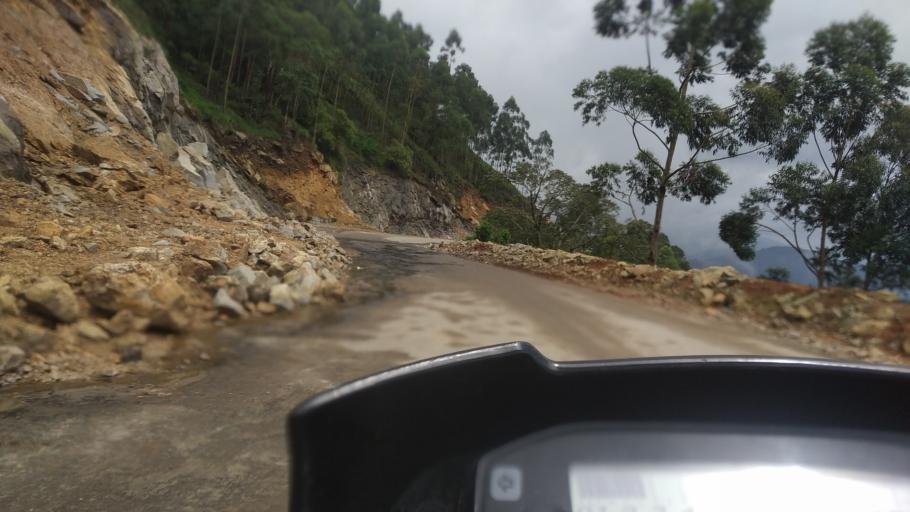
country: IN
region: Kerala
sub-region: Idukki
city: Munnar
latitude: 10.0368
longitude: 77.1337
